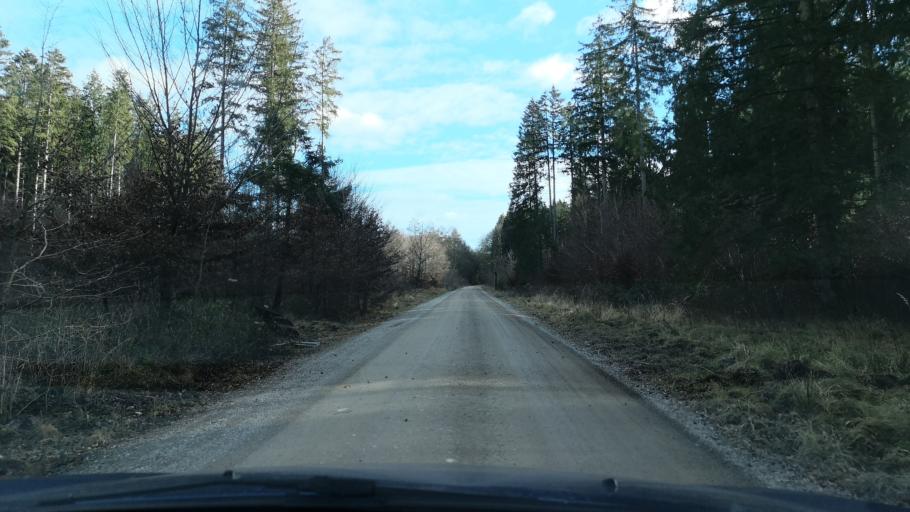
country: DE
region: Bavaria
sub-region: Upper Bavaria
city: Kirchseeon
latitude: 48.1112
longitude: 11.9190
